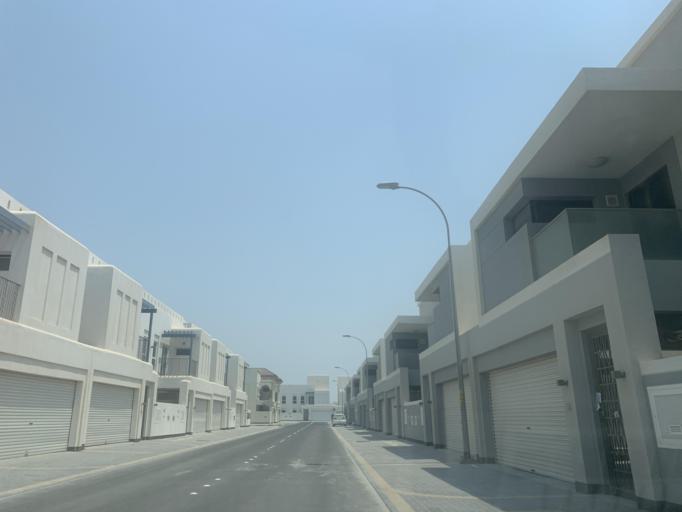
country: BH
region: Muharraq
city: Al Muharraq
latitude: 26.3130
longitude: 50.6230
